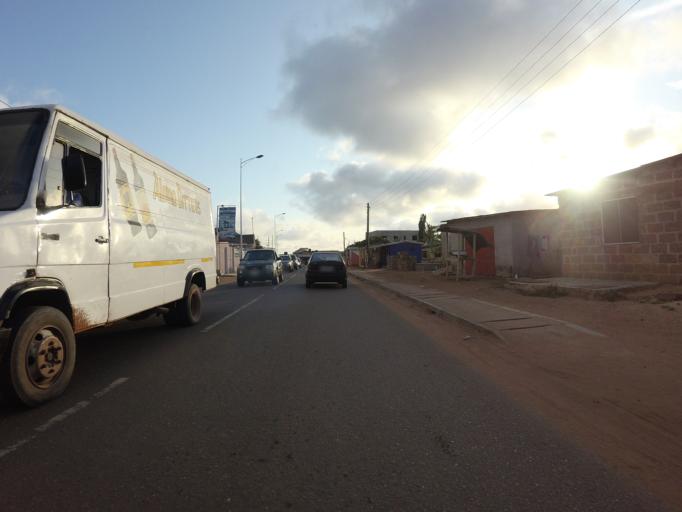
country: GH
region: Greater Accra
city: Teshi Old Town
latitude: 5.5952
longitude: -0.1273
